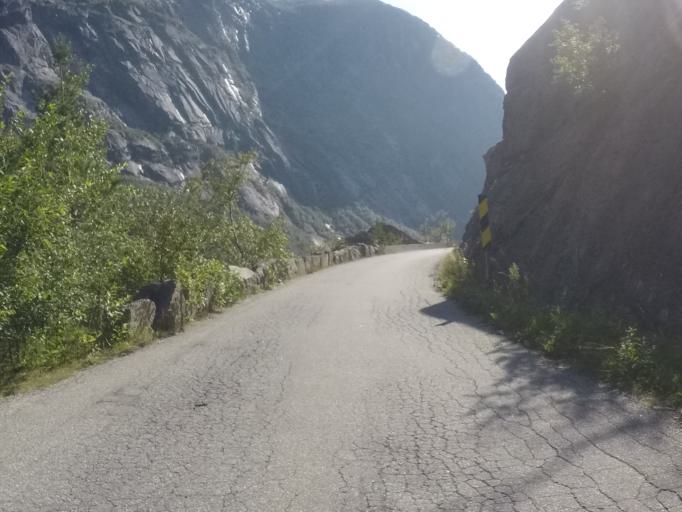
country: NO
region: Hordaland
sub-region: Odda
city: Odda
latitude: 60.1203
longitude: 6.5878
